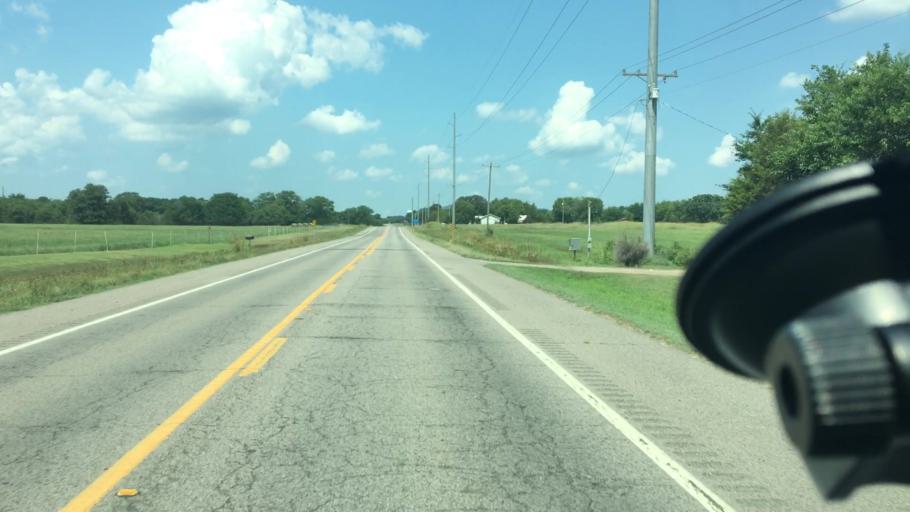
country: US
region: Arkansas
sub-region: Logan County
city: Paris
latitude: 35.2949
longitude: -93.6700
